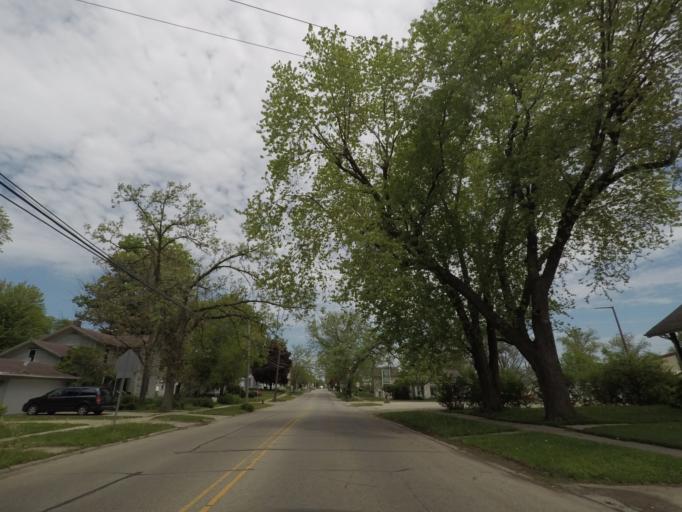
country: US
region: Wisconsin
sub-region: Rock County
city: Evansville
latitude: 42.7771
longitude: -89.2991
